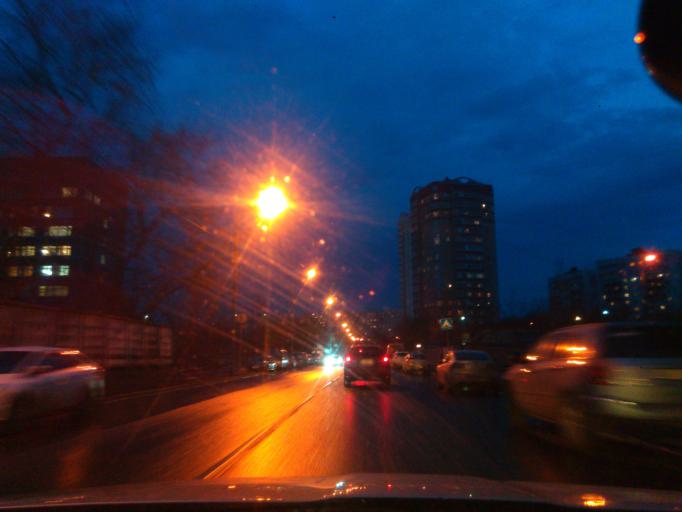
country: RU
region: Moscow
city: Zapadnoye Degunino
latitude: 55.8692
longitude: 37.5270
